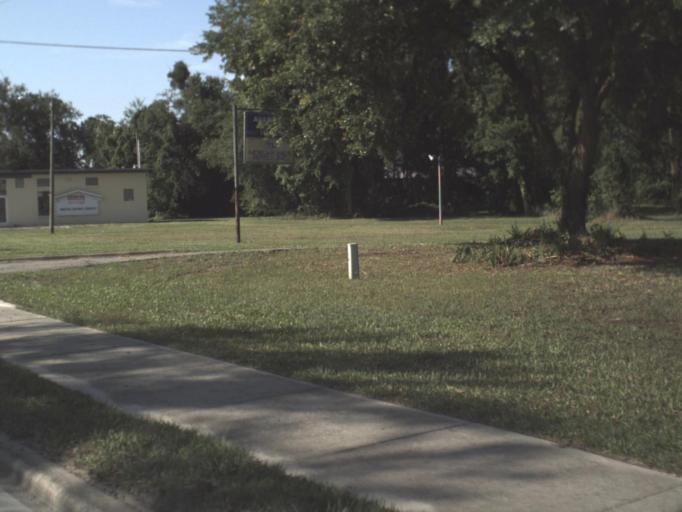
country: US
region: Florida
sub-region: Alachua County
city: Gainesville
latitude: 29.6993
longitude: -82.3396
